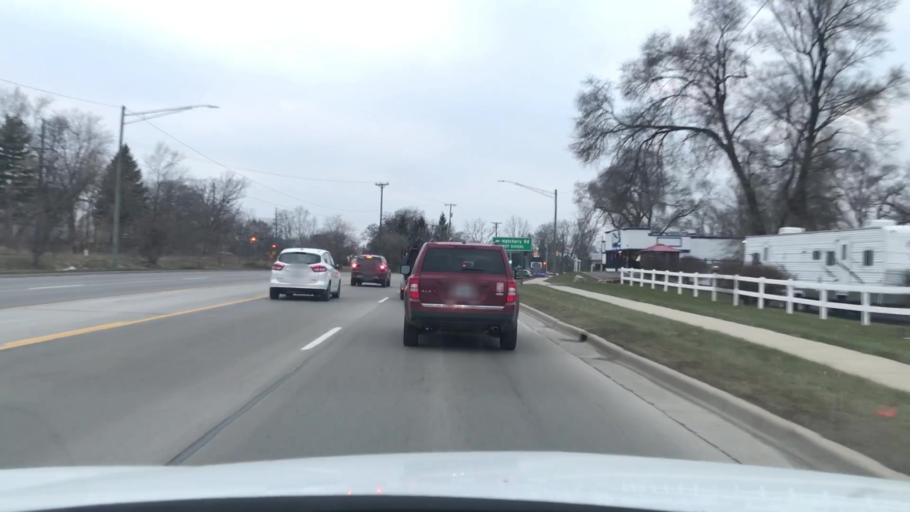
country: US
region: Michigan
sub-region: Oakland County
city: Waterford
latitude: 42.6791
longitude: -83.3695
